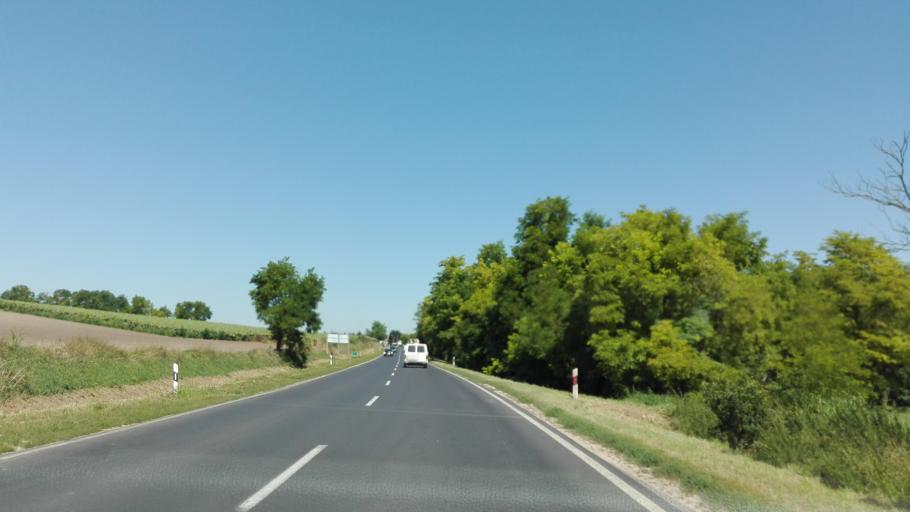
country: HU
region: Fejer
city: Mezoszilas
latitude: 46.8021
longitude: 18.4891
